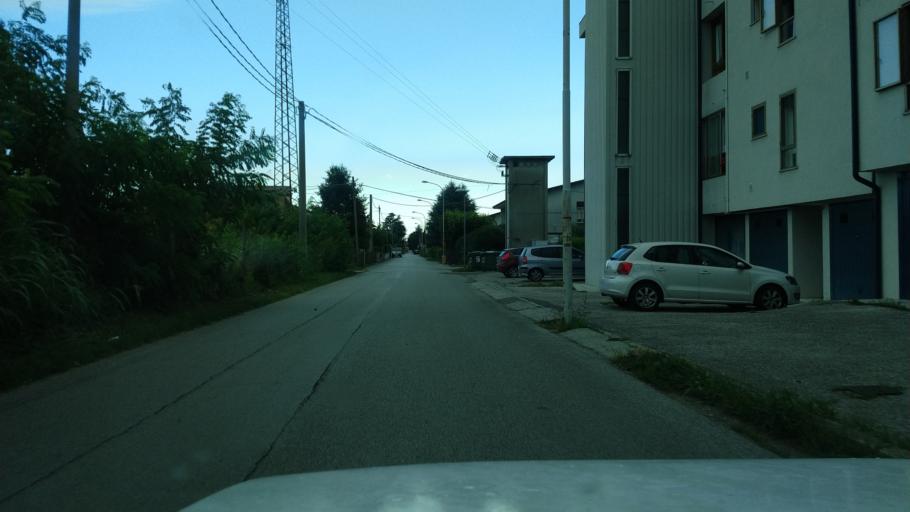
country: IT
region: Veneto
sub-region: Provincia di Vicenza
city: Bassano del Grappa
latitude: 45.7528
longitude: 11.6998
